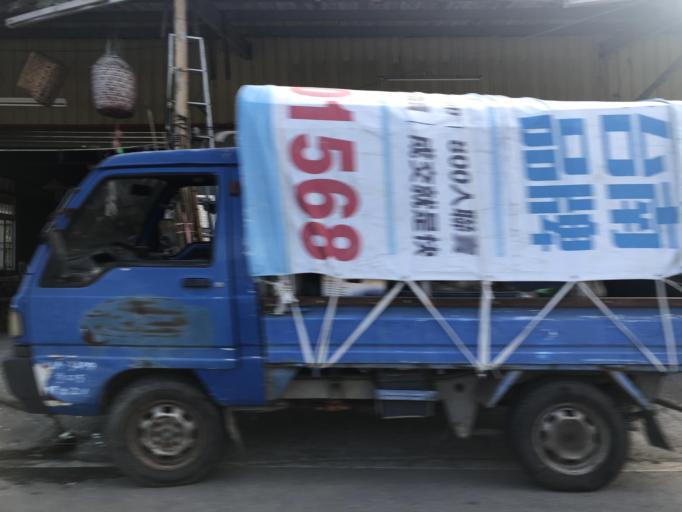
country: TW
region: Taiwan
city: Yujing
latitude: 23.0535
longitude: 120.4113
